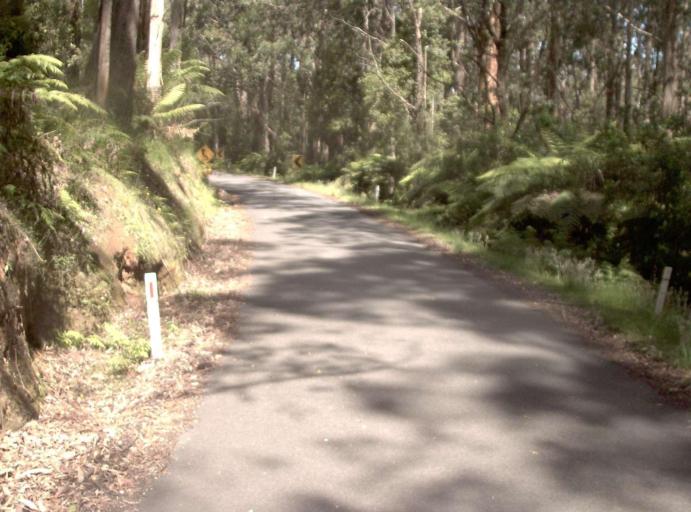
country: AU
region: Victoria
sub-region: Baw Baw
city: Warragul
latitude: -37.8625
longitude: 146.1138
